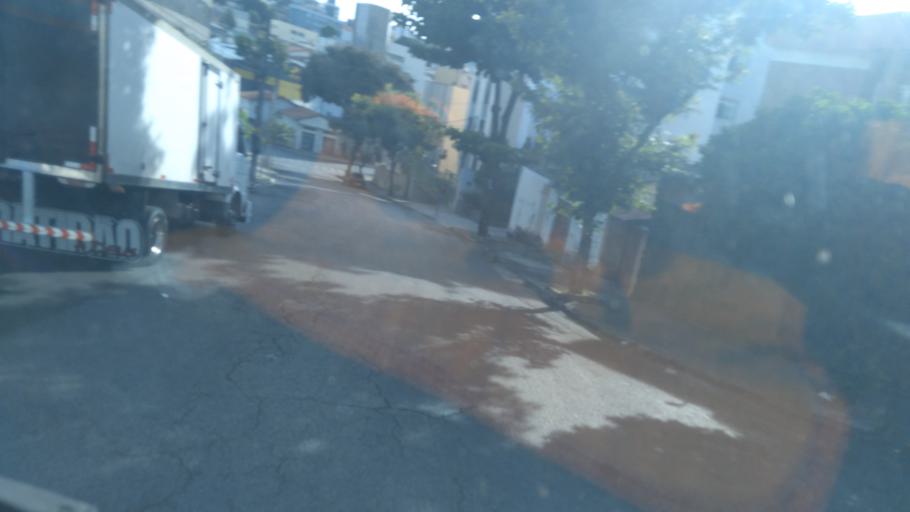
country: BR
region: Minas Gerais
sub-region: Belo Horizonte
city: Belo Horizonte
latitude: -19.8839
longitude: -43.9276
